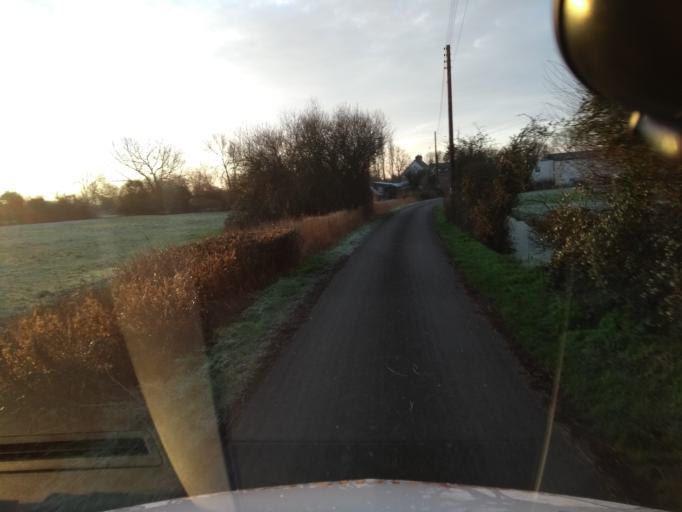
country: GB
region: England
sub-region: Somerset
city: Highbridge
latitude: 51.2216
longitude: -2.9299
